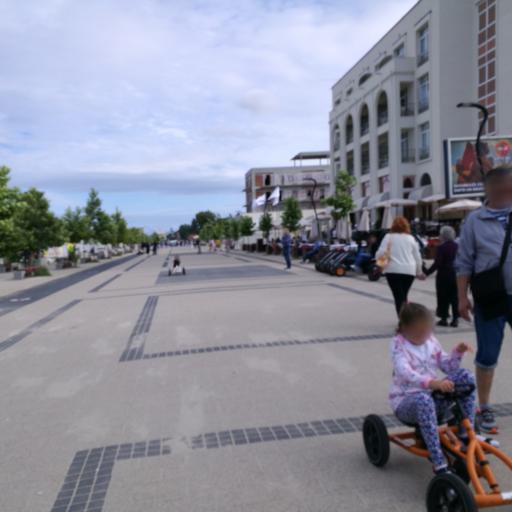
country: RO
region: Constanta
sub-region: Municipiul Constanta
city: Palazu Mare
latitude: 44.2445
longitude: 28.6228
